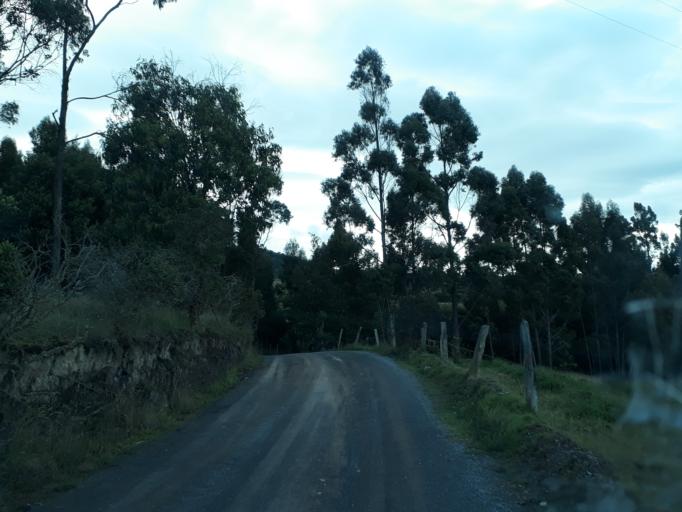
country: CO
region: Cundinamarca
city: Carmen de Carupa
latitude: 5.3321
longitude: -73.9097
